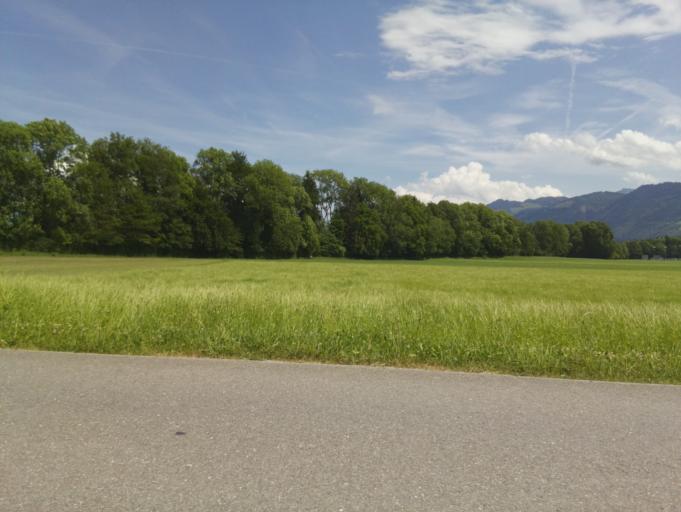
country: CH
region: Schwyz
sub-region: Bezirk March
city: Lachen
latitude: 47.2000
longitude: 8.8610
